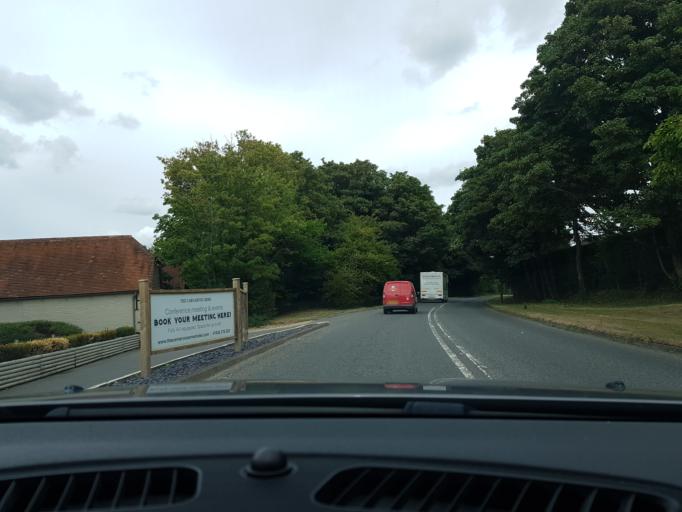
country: GB
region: England
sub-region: Hampshire
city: Highclere
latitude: 51.3339
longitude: -1.3442
